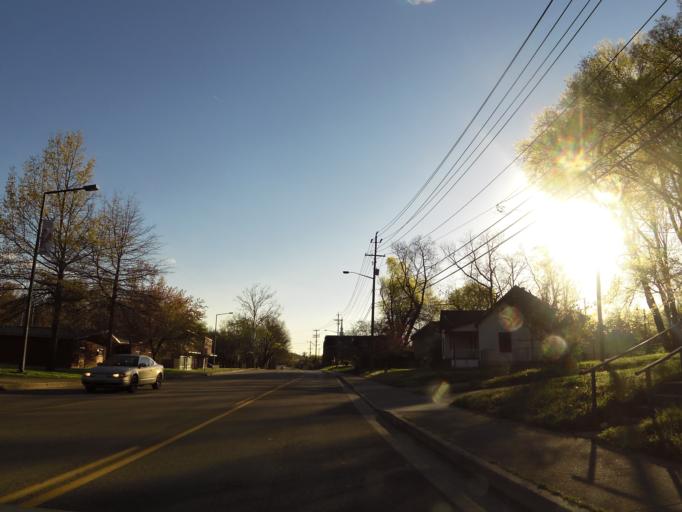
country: US
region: Tennessee
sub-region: Knox County
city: Knoxville
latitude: 35.9784
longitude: -83.8986
